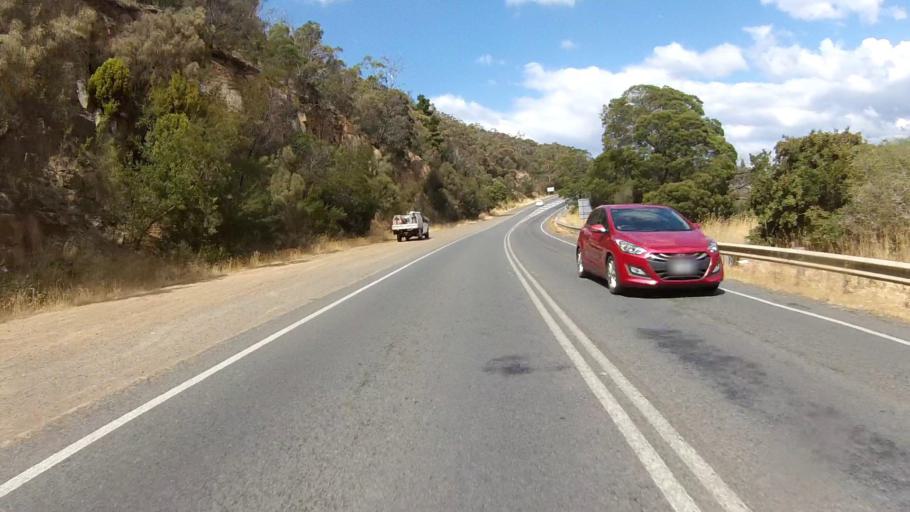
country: AU
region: Tasmania
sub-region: Brighton
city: Old Beach
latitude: -42.7889
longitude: 147.2925
